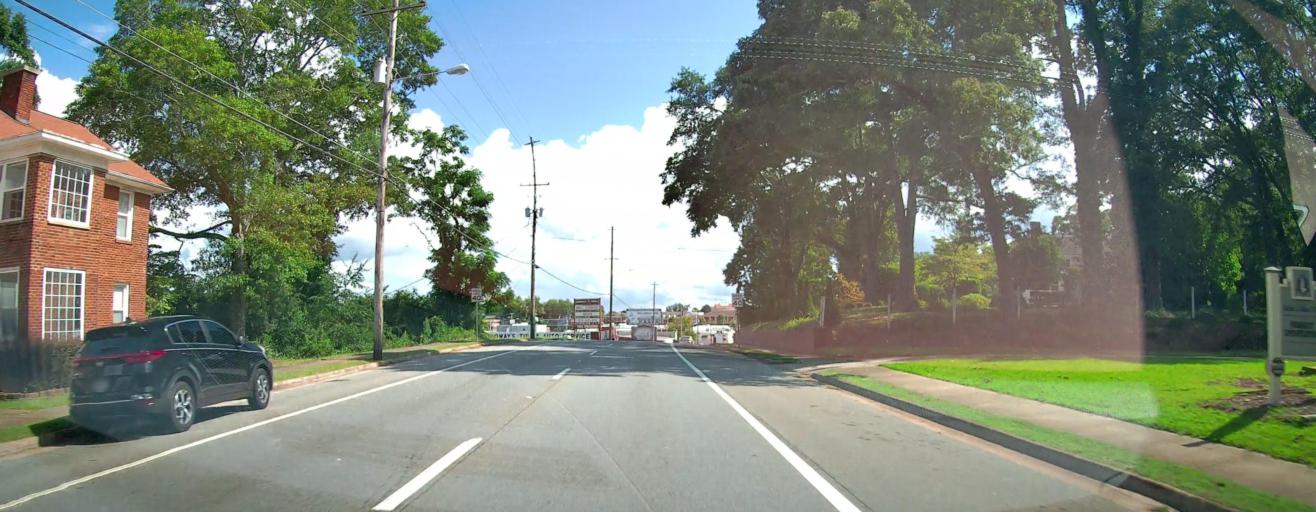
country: US
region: Georgia
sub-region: Upson County
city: Thomaston
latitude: 32.8946
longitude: -84.3274
